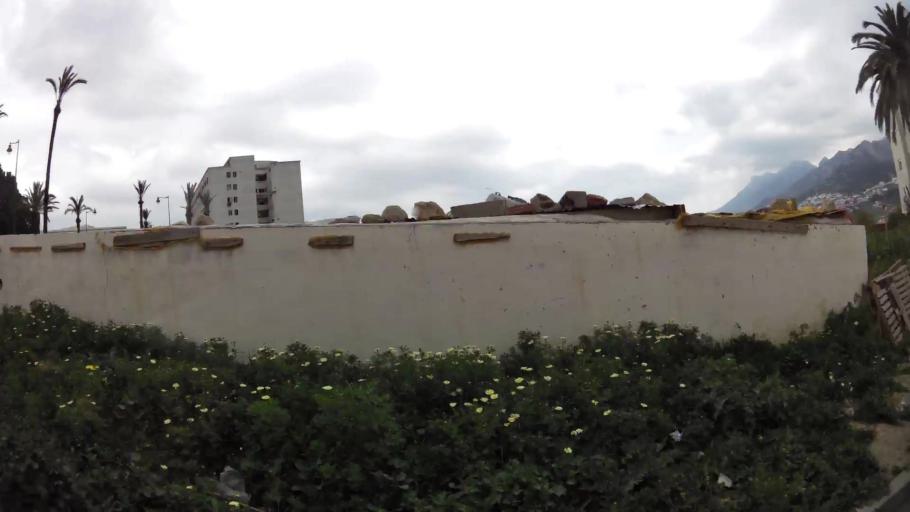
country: MA
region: Tanger-Tetouan
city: Tetouan
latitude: 35.5679
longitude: -5.3785
